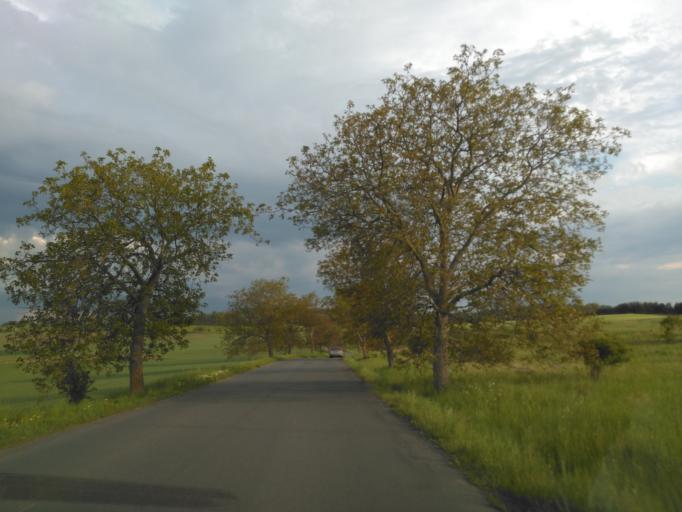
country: CZ
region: Central Bohemia
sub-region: Okres Beroun
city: Beroun
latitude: 49.9348
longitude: 14.0729
